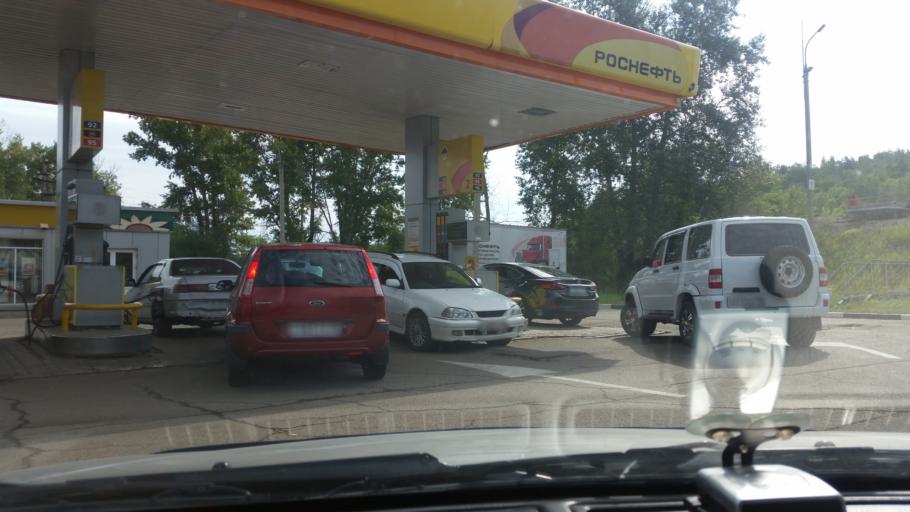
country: RU
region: Irkutsk
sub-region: Irkutskiy Rayon
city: Irkutsk
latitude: 52.3319
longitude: 104.3173
